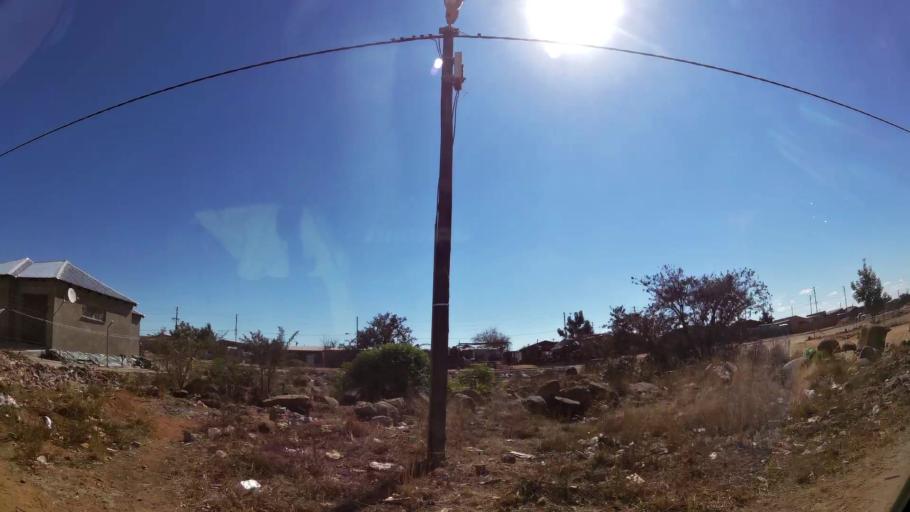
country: ZA
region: Limpopo
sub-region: Capricorn District Municipality
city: Polokwane
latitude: -23.8946
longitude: 29.4175
